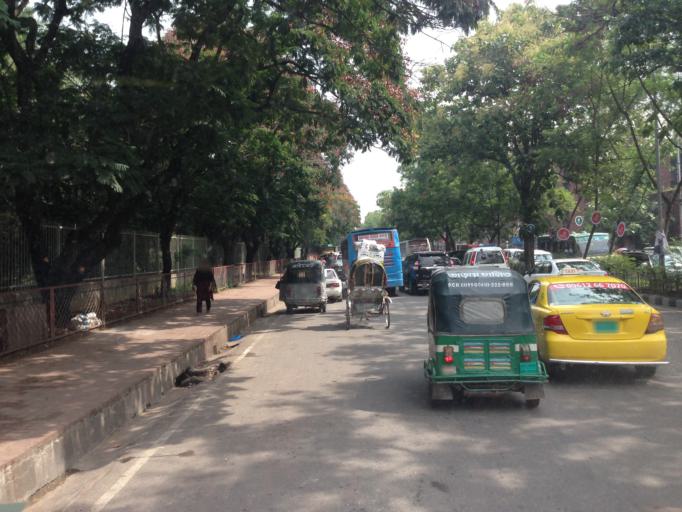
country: BD
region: Dhaka
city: Azimpur
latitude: 23.7592
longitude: 90.3837
